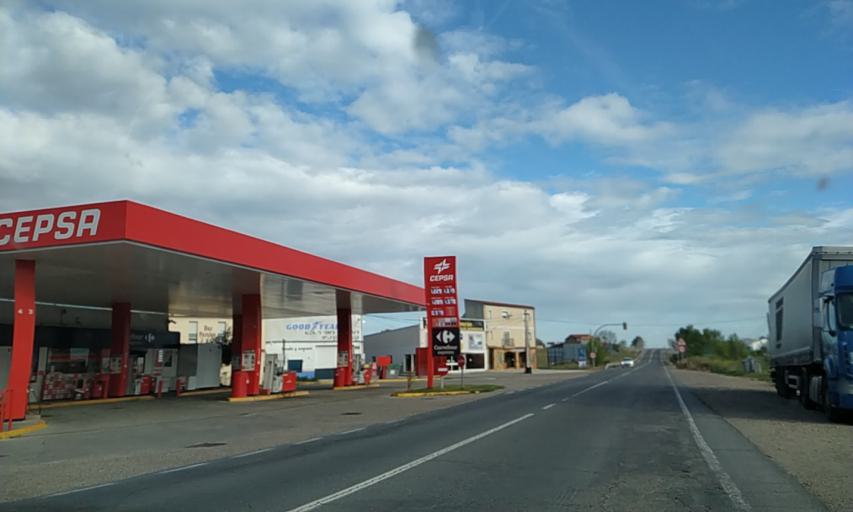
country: ES
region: Extremadura
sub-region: Provincia de Caceres
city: Moraleja
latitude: 40.0636
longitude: -6.6516
